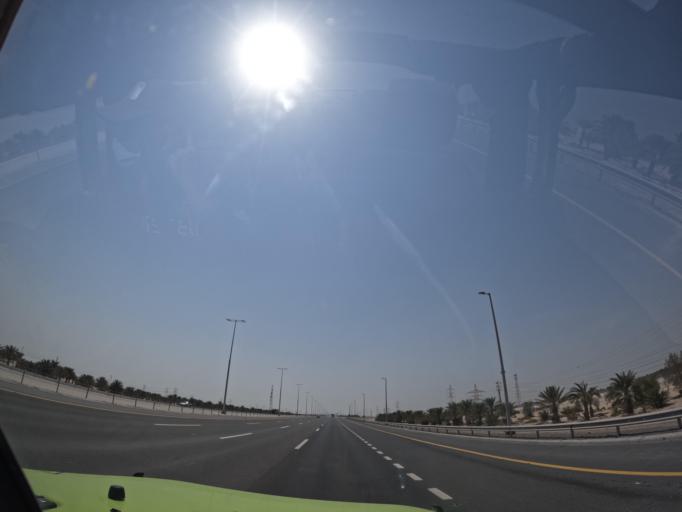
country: AE
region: Abu Dhabi
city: Abu Dhabi
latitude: 24.1805
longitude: 54.3730
